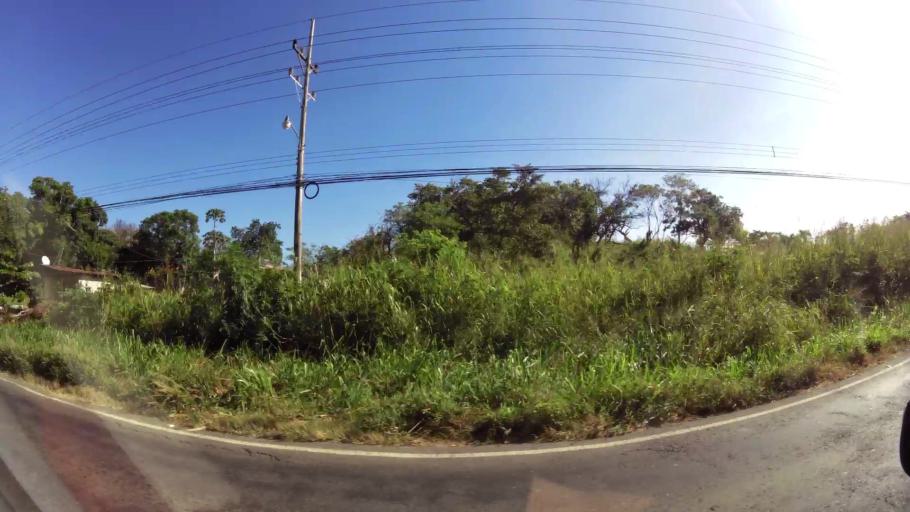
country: CR
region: Guanacaste
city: Sardinal
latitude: 10.5818
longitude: -85.5683
